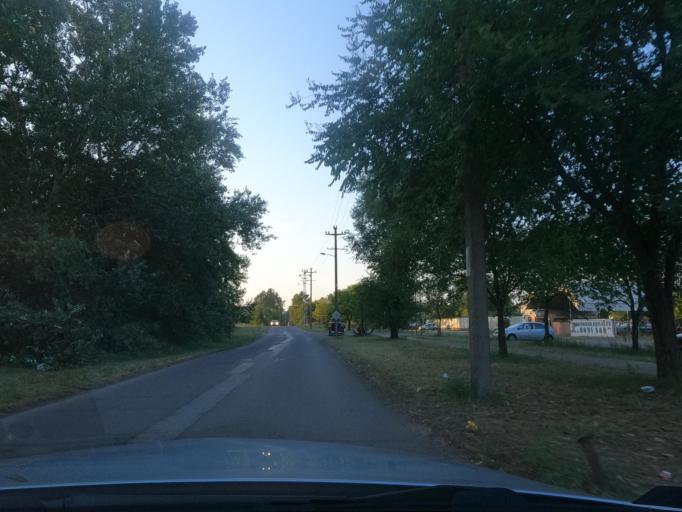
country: RS
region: Autonomna Pokrajina Vojvodina
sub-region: Juznobacki Okrug
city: Novi Sad
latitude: 45.2315
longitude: 19.8276
